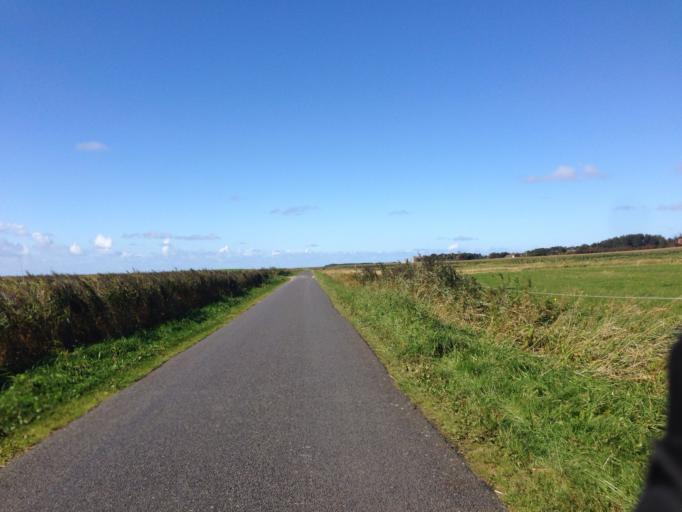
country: DE
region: Schleswig-Holstein
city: Borgsum
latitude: 54.6946
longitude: 8.4505
